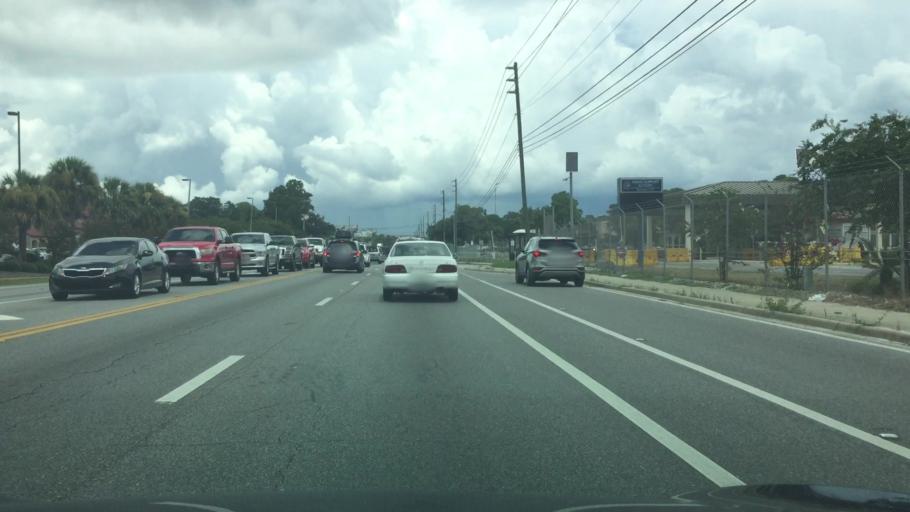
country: US
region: Florida
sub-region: Bay County
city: Upper Grand Lagoon
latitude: 30.1752
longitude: -85.7600
